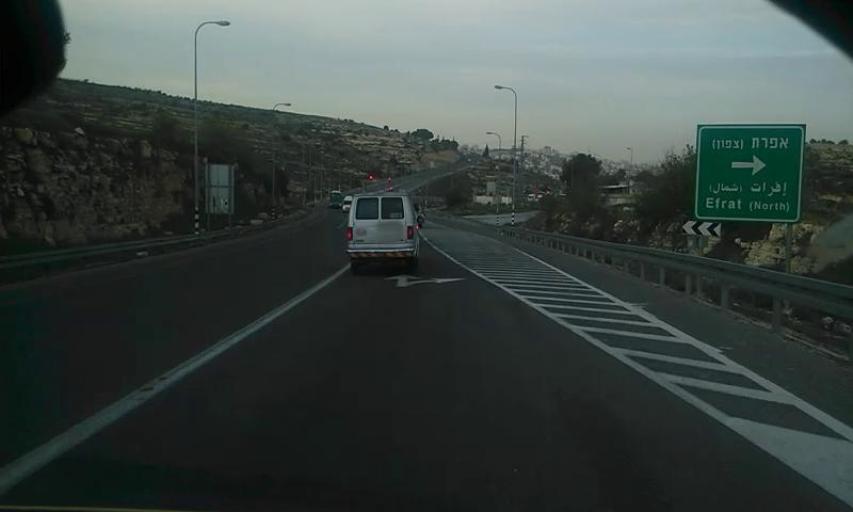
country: PS
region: West Bank
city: Al Khadir
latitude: 31.6846
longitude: 35.1587
